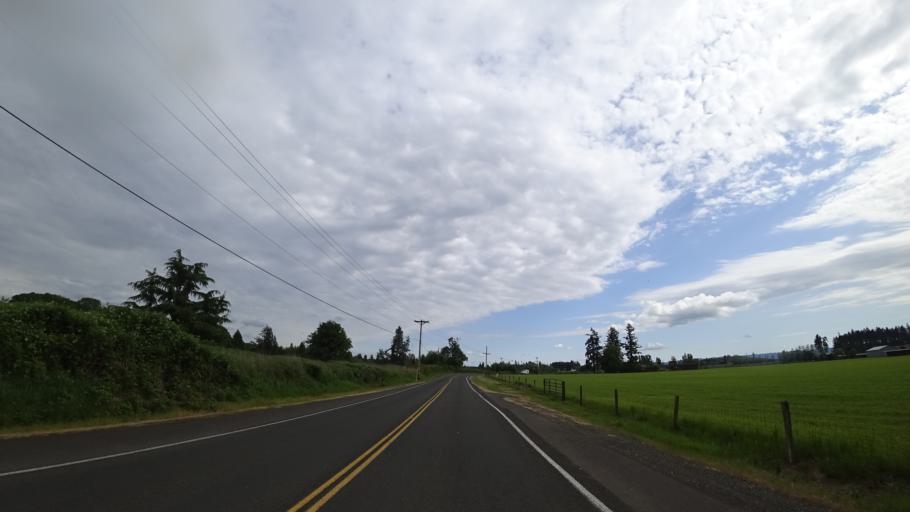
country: US
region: Oregon
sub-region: Washington County
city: Hillsboro
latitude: 45.4879
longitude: -122.9505
